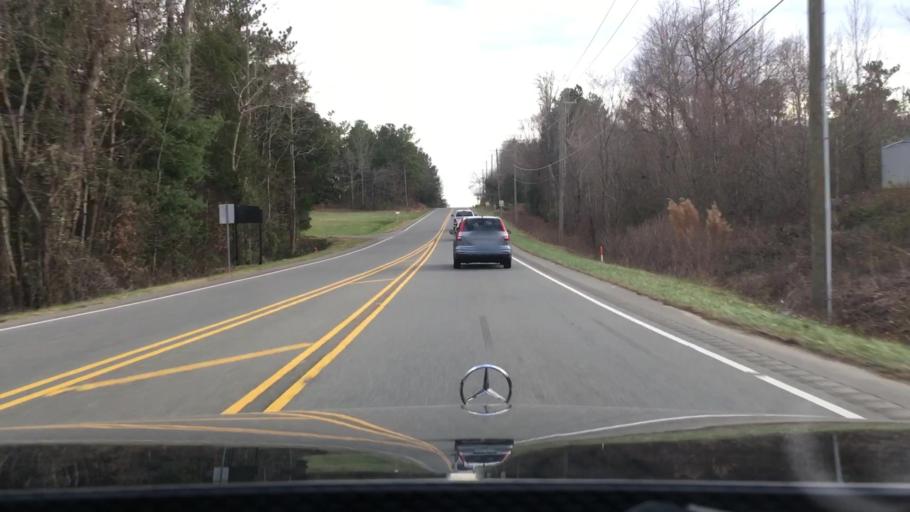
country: US
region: North Carolina
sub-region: Orange County
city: Hillsborough
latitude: 36.0981
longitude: -79.1066
